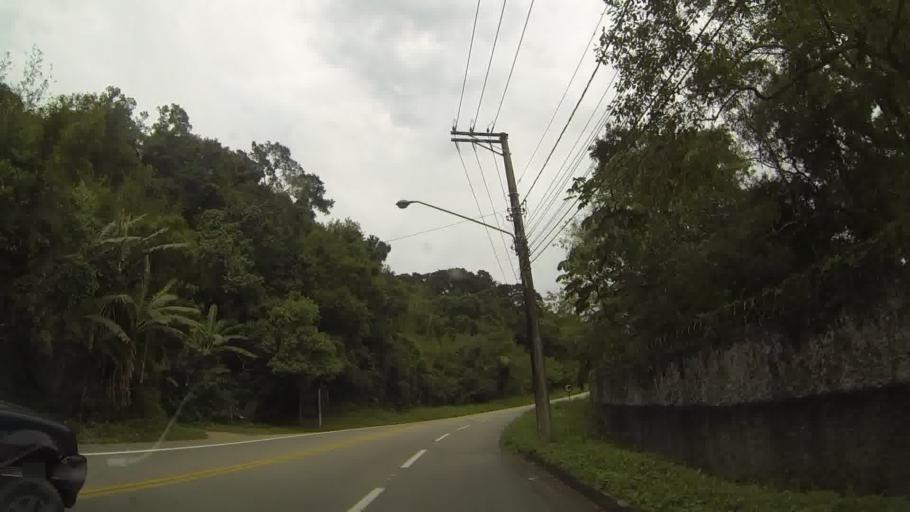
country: BR
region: Sao Paulo
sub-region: Sao Sebastiao
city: Sao Sebastiao
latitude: -23.8169
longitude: -45.5271
